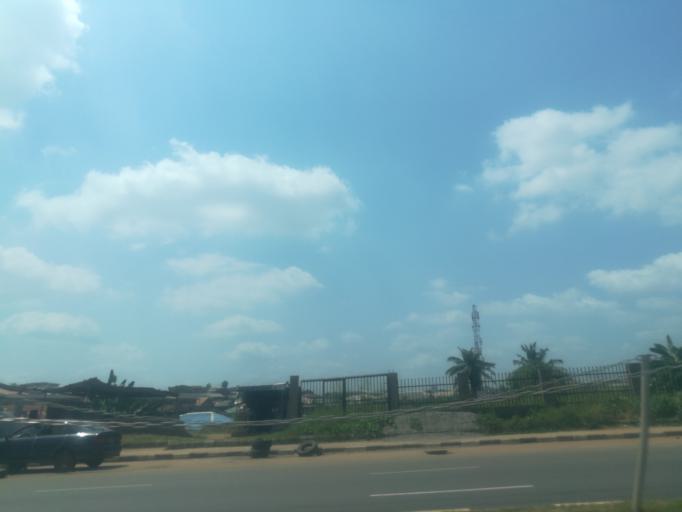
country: NG
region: Ogun
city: Abeokuta
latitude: 7.1416
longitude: 3.3639
